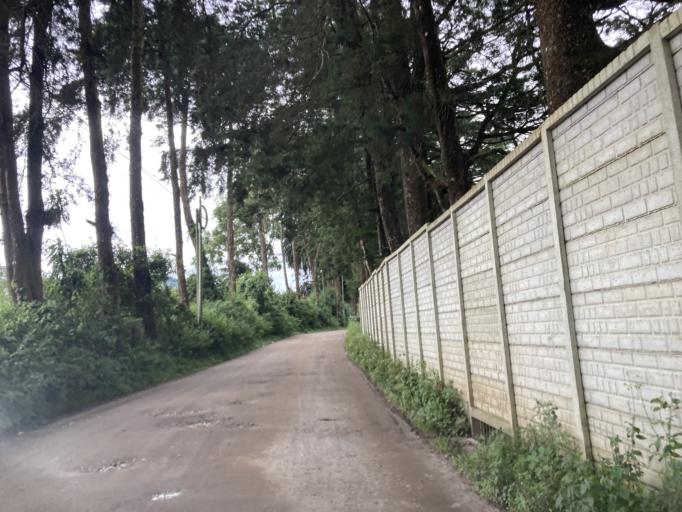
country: GT
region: Guatemala
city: San Jose Pinula
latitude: 14.5320
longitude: -90.4050
